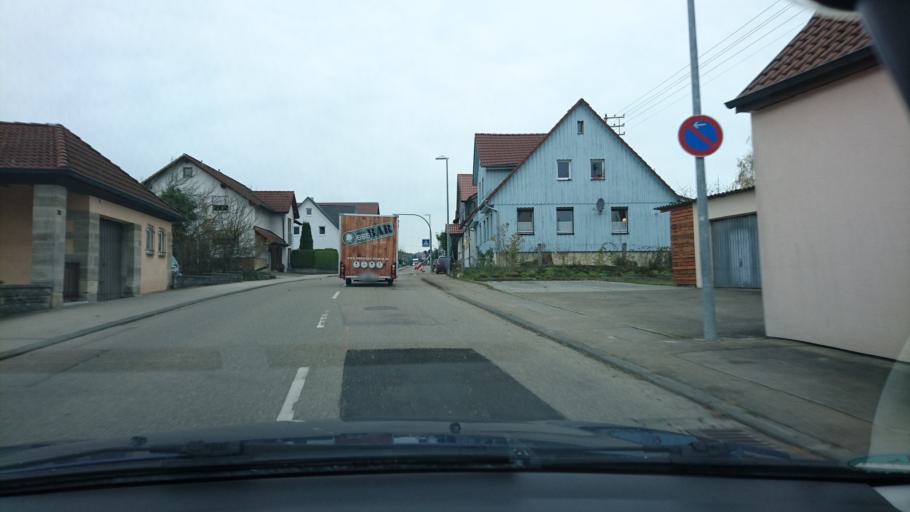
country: DE
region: Baden-Wuerttemberg
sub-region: Regierungsbezirk Stuttgart
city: Gschwend
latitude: 48.9345
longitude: 9.7396
